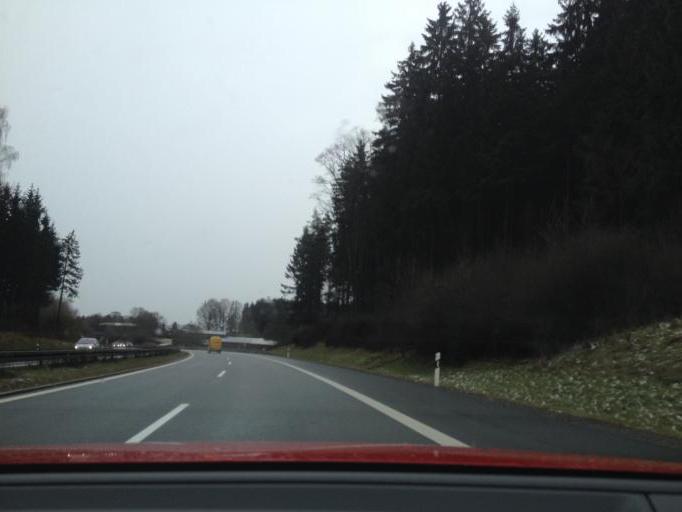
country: DE
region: Bavaria
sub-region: Upper Franconia
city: Schonwald
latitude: 50.1925
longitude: 12.1010
